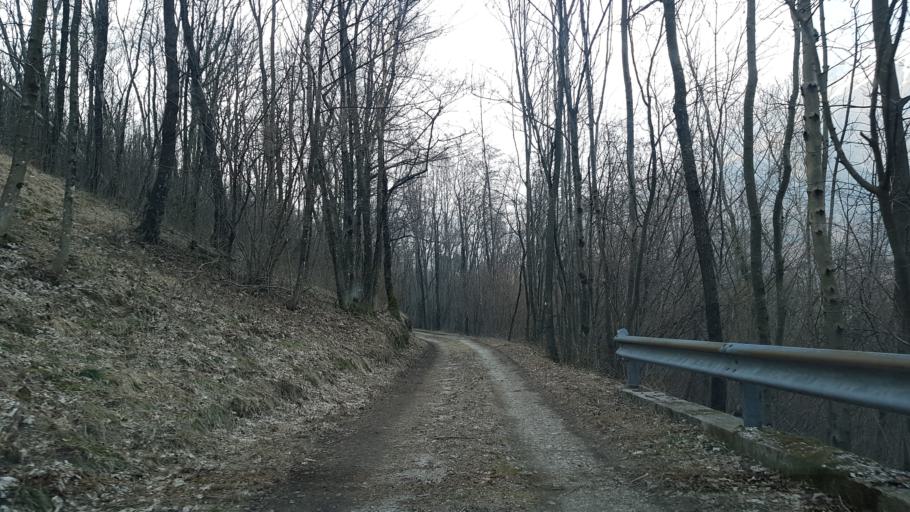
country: IT
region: Friuli Venezia Giulia
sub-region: Provincia di Udine
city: Lusevera
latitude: 46.2655
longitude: 13.2984
